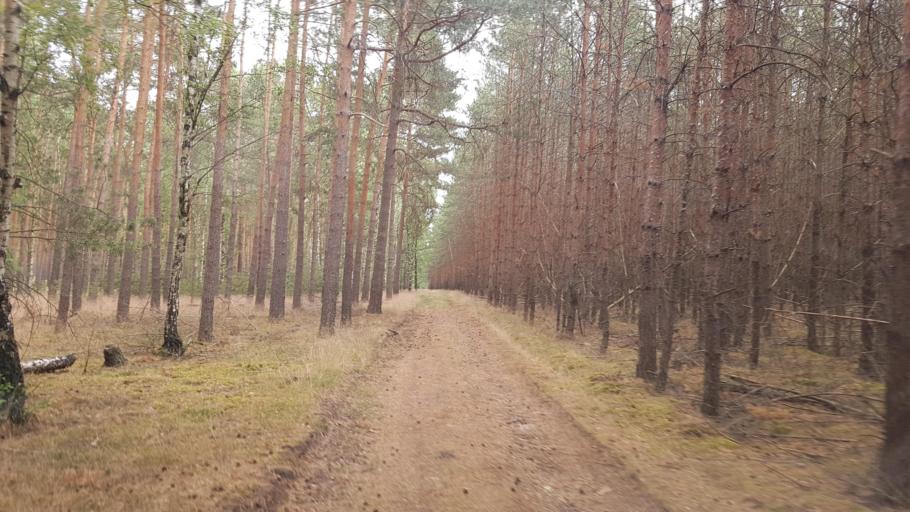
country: DE
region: Brandenburg
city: Treuenbrietzen
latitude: 52.0567
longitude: 12.8144
